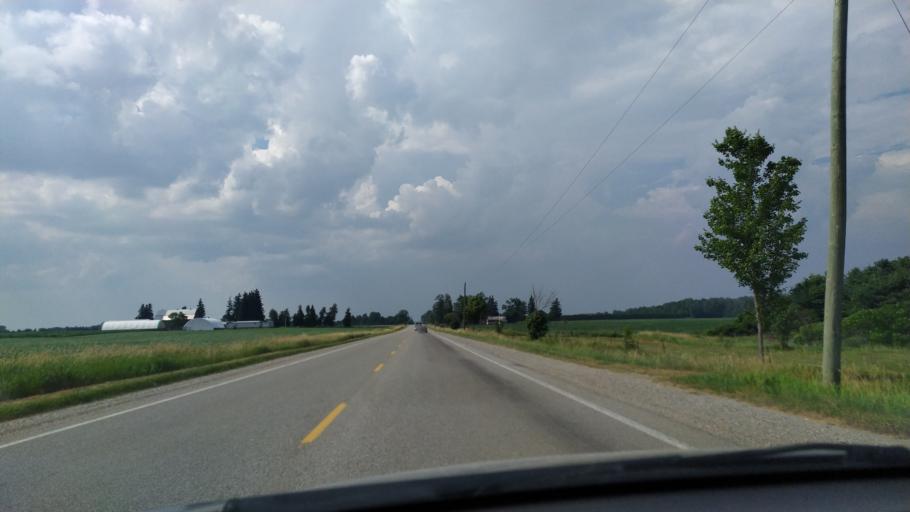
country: CA
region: Ontario
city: Dorchester
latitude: 43.0299
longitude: -81.1204
